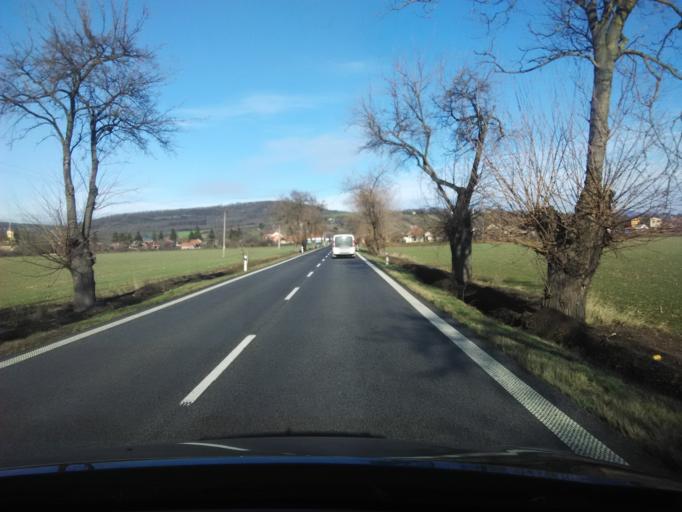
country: SK
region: Nitriansky
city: Tlmace
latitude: 48.2687
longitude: 18.5118
